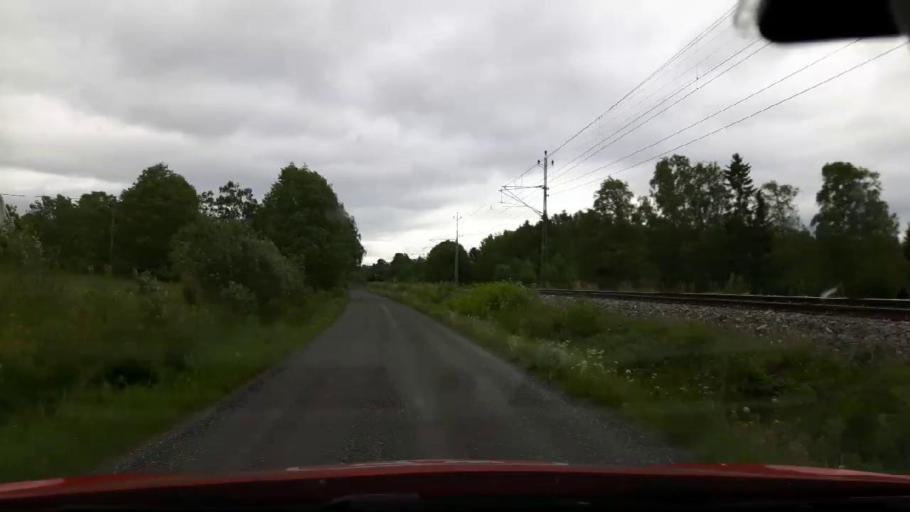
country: SE
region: Jaemtland
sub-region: Krokoms Kommun
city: Krokom
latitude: 63.2485
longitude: 14.5258
